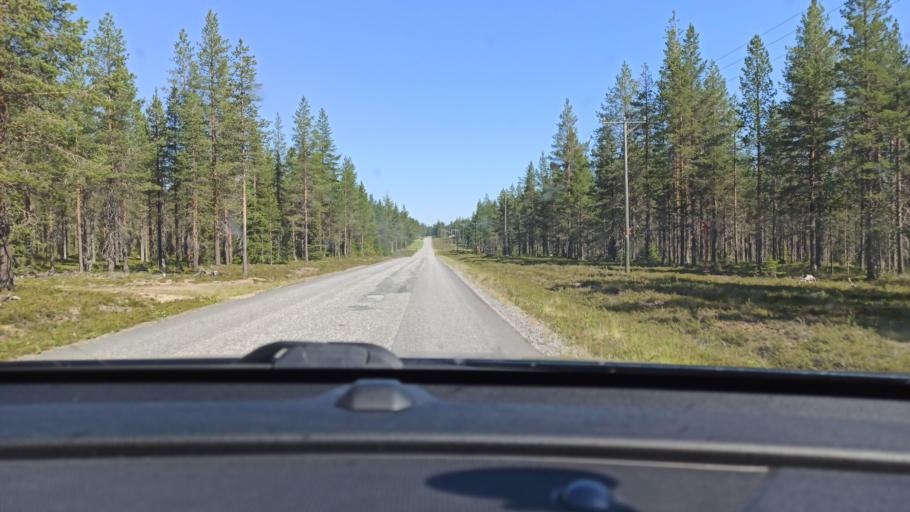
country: FI
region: Lapland
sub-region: Tunturi-Lappi
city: Kolari
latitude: 67.6499
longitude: 24.1617
